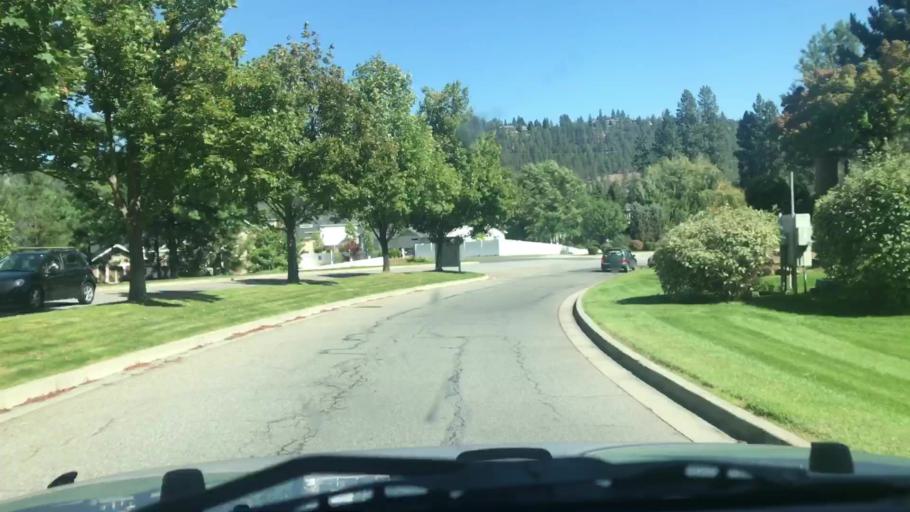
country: US
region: Washington
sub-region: Spokane County
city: Spokane
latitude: 47.5981
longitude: -117.4142
